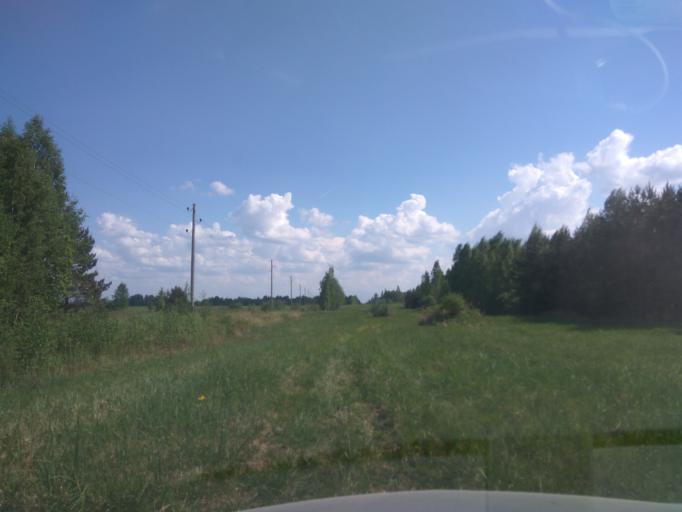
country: LV
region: Kuldigas Rajons
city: Kuldiga
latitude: 57.1795
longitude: 22.0055
